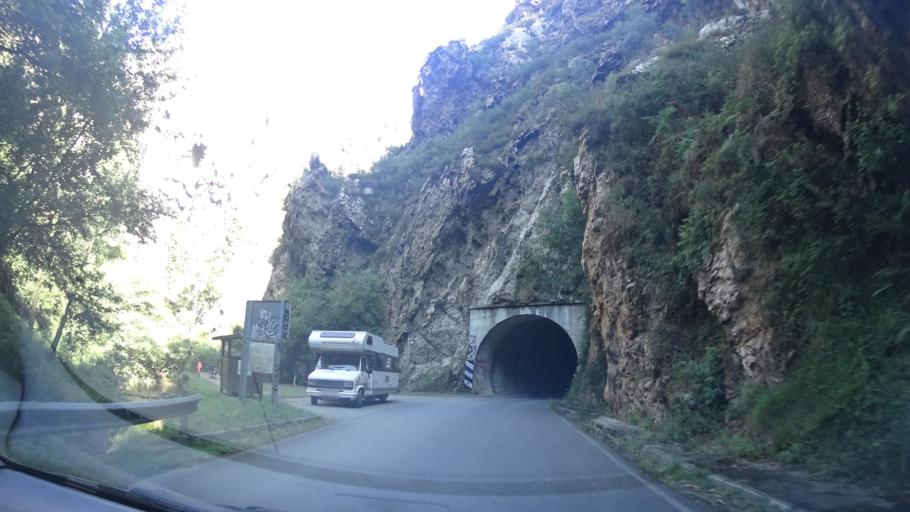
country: ES
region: Asturias
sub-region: Province of Asturias
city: Ribadesella
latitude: 43.4722
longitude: -5.1323
